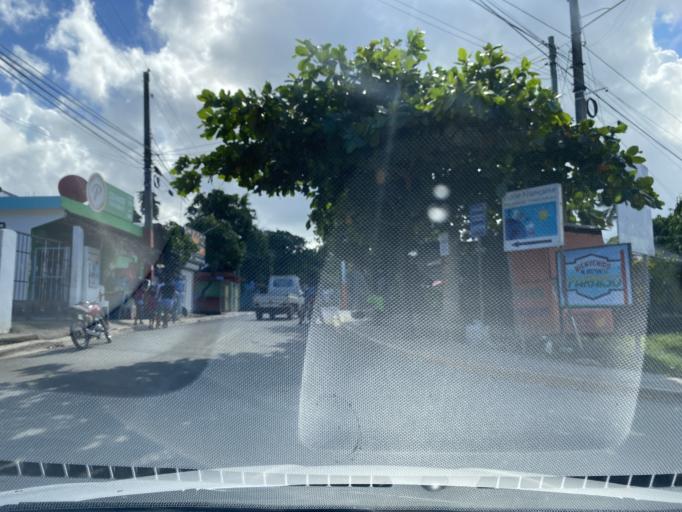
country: DO
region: Samana
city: Las Terrenas
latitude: 19.3056
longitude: -69.5416
